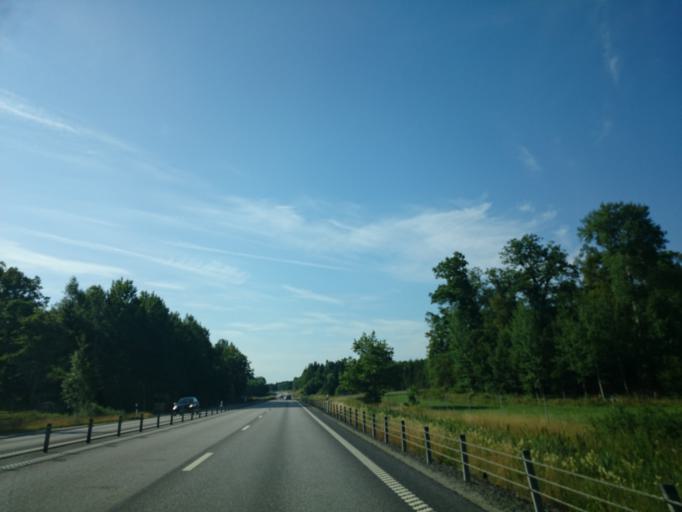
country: SE
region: OEstergoetland
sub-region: Valdemarsviks Kommun
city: Gusum
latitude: 58.3773
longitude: 16.4231
